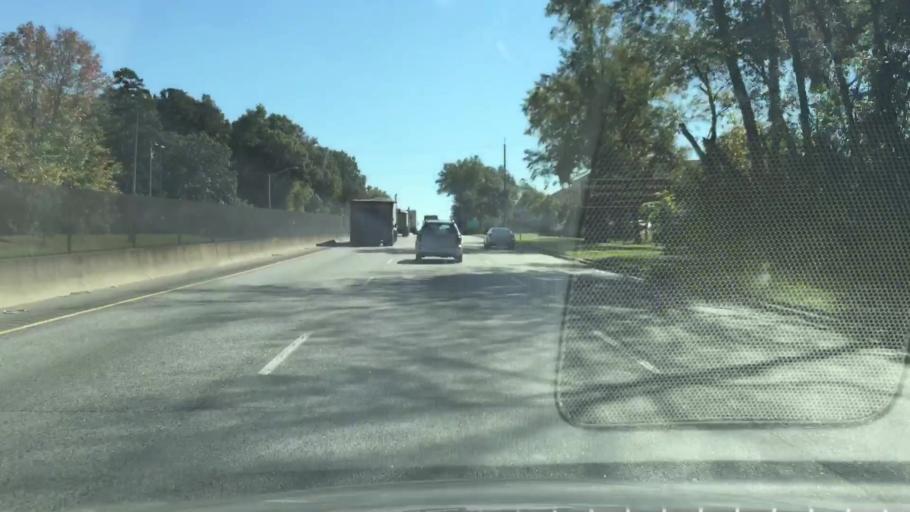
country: US
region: North Carolina
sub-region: Guilford County
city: Greensboro
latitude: 36.0794
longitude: -79.7672
